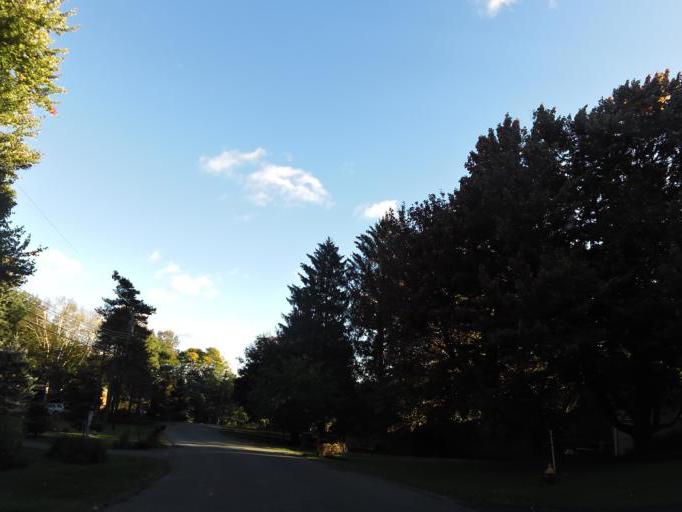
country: US
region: New York
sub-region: Erie County
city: Elma Center
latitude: 42.8241
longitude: -78.6265
